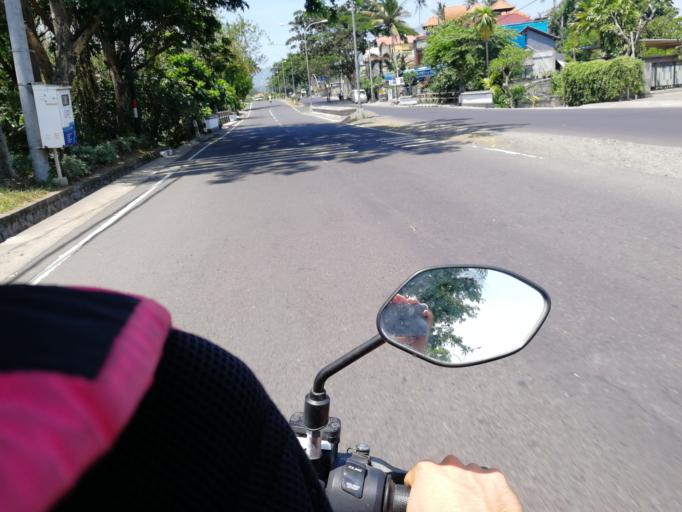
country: ID
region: Bali
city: Subagan
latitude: -8.4411
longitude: 115.5917
